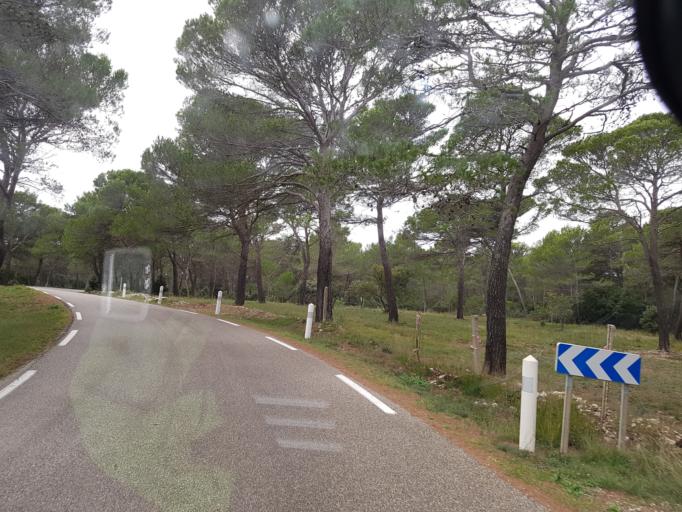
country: FR
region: Provence-Alpes-Cote d'Azur
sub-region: Departement des Bouches-du-Rhone
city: Cuges-les-Pins
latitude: 43.2518
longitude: 5.7345
